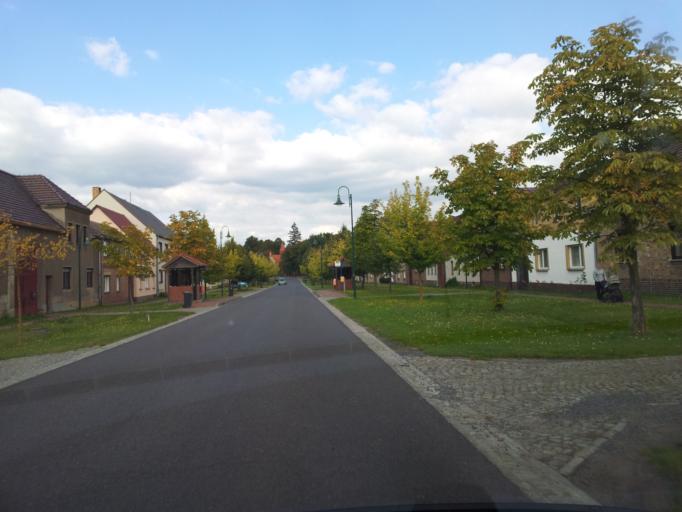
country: DE
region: Brandenburg
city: Sallgast
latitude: 51.5968
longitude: 13.7783
